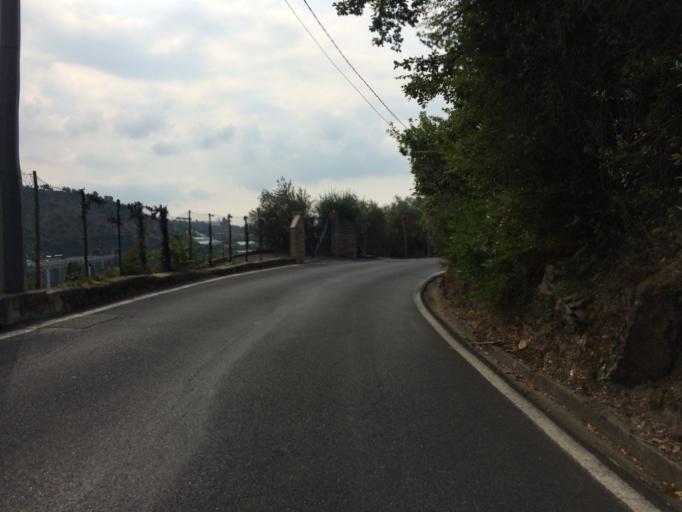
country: IT
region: Liguria
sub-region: Provincia di Imperia
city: San Remo
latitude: 43.8373
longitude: 7.7565
